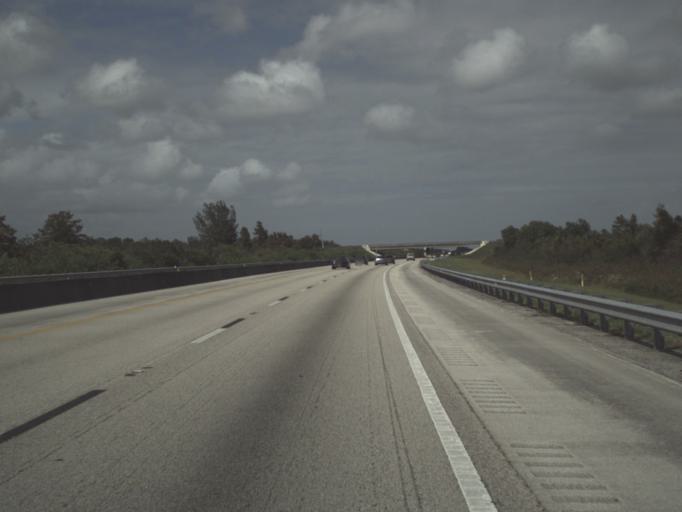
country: US
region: Florida
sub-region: Martin County
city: Hobe Sound
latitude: 27.0396
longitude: -80.2392
